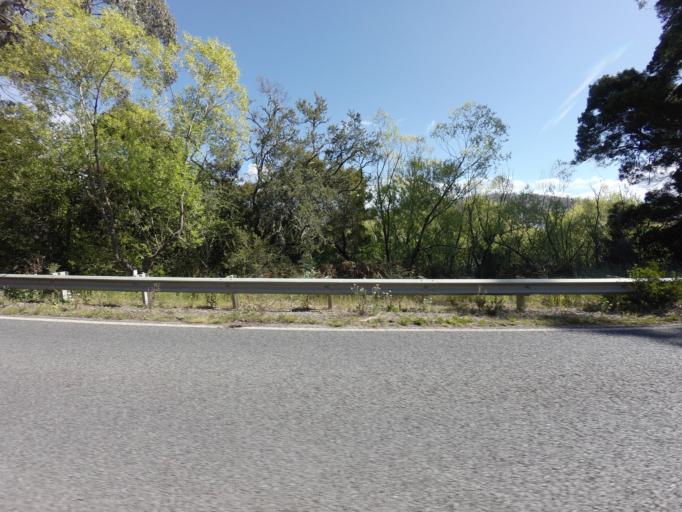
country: AU
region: Tasmania
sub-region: Derwent Valley
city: New Norfolk
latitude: -42.7677
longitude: 147.0257
